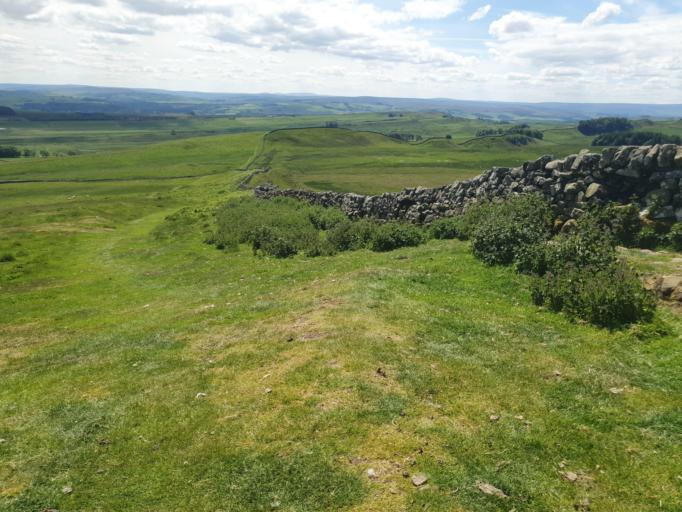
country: GB
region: England
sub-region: Northumberland
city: Bardon Mill
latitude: 55.0238
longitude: -2.3151
